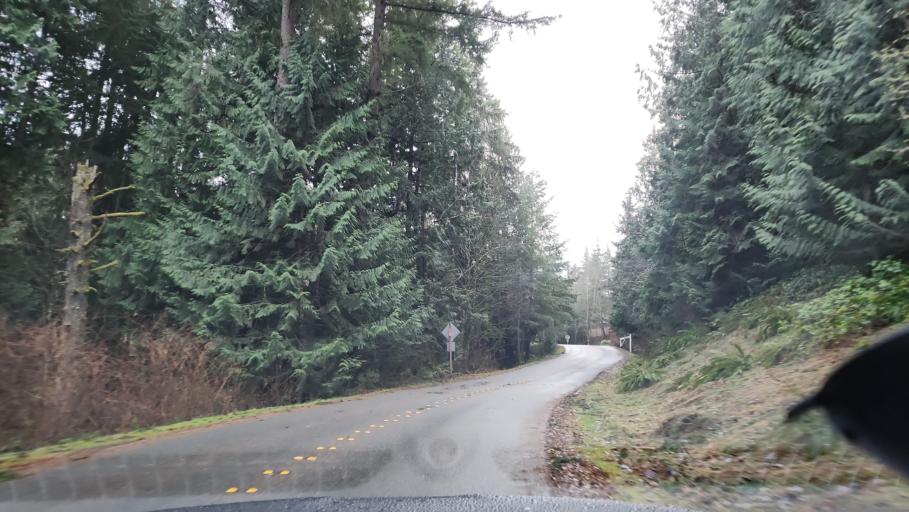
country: US
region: Washington
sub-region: King County
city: Union Hill-Novelty Hill
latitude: 47.6944
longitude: -122.0493
